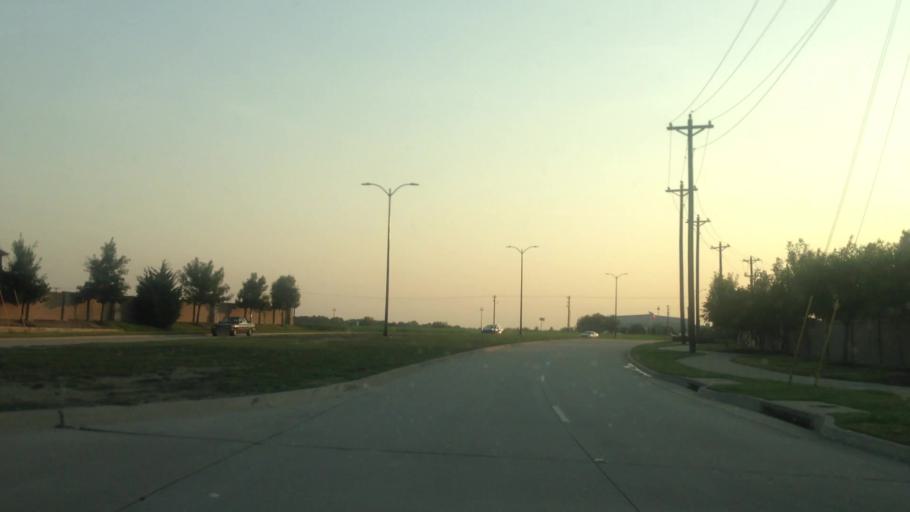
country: US
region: Texas
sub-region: Denton County
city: The Colony
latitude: 33.1147
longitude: -96.8888
